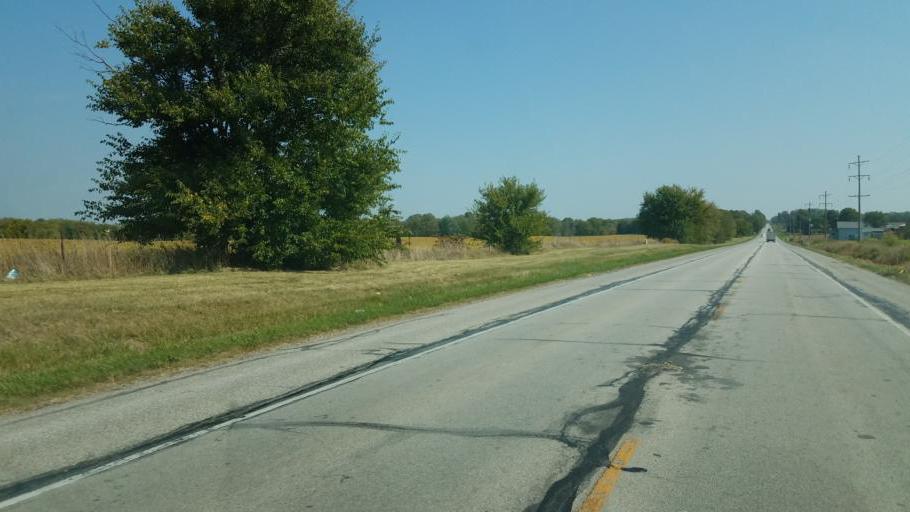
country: US
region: Indiana
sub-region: LaGrange County
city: Lagrange
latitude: 41.6411
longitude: -85.4672
